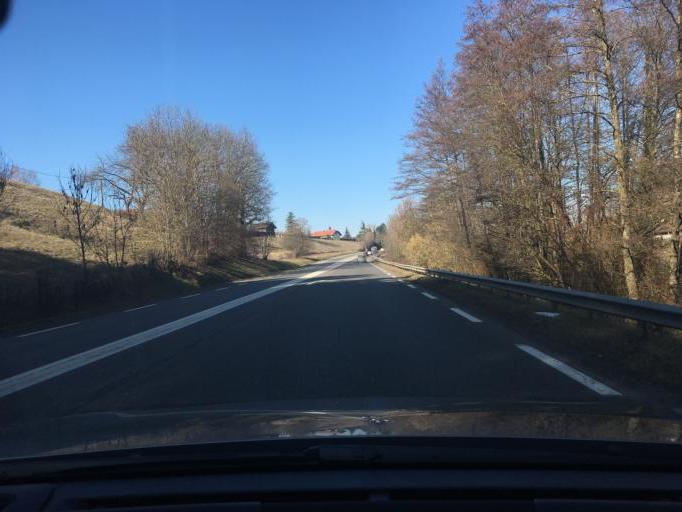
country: FR
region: Rhone-Alpes
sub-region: Departement de la Haute-Savoie
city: Cranves-Sales
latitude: 46.1942
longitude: 6.2923
